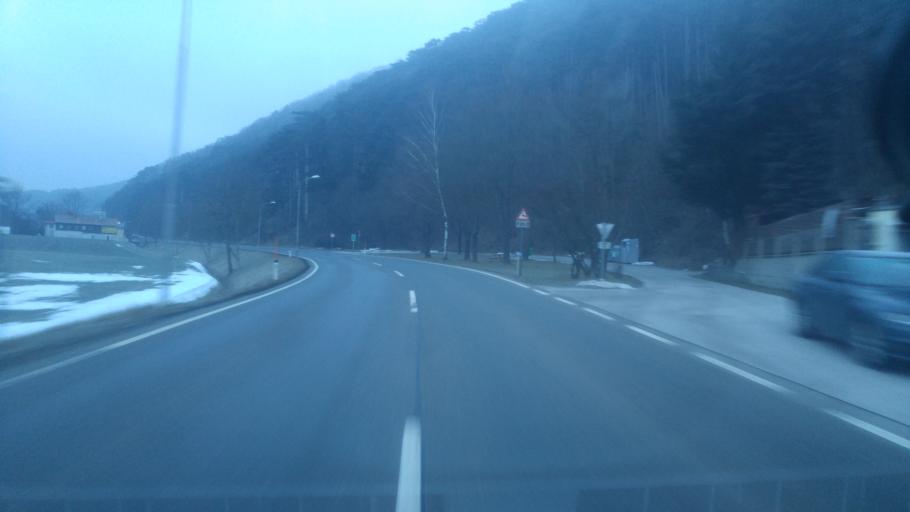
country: AT
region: Lower Austria
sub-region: Politischer Bezirk Baden
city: Weissenbach an der Triesting
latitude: 47.9832
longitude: 16.0609
